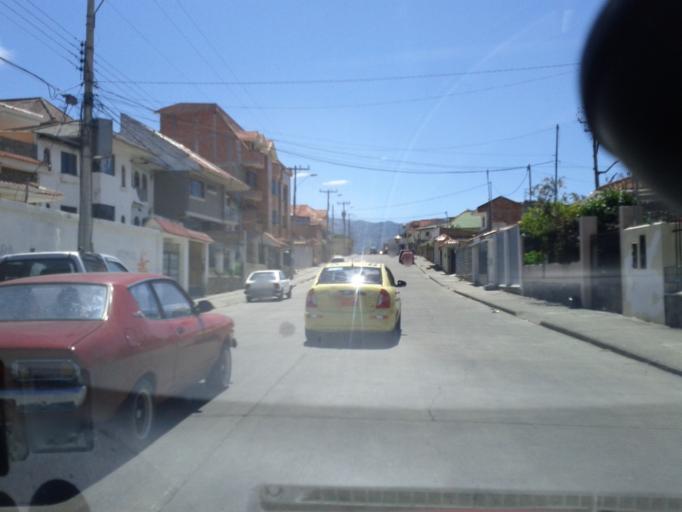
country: EC
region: Azuay
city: Cuenca
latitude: -2.9070
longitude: -79.0167
